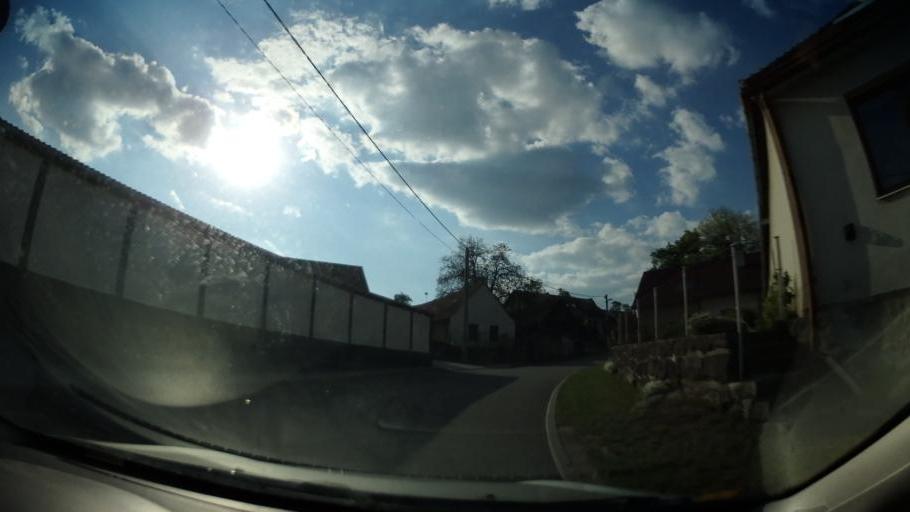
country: CZ
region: Vysocina
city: Budisov
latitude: 49.2944
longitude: 15.9820
